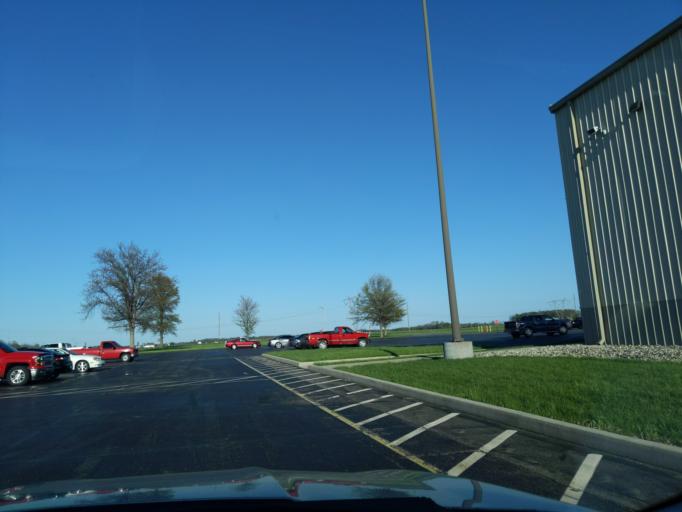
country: US
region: Indiana
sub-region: Decatur County
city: Westport
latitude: 39.2085
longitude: -85.5772
